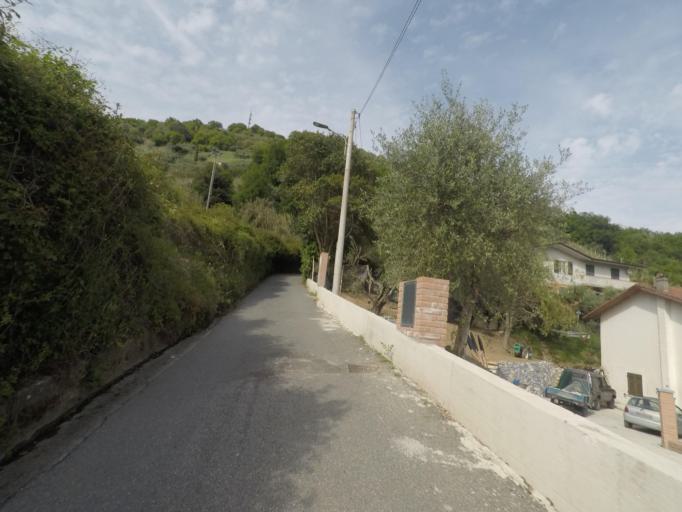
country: IT
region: Tuscany
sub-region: Provincia di Massa-Carrara
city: Massa
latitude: 44.0482
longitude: 10.0992
